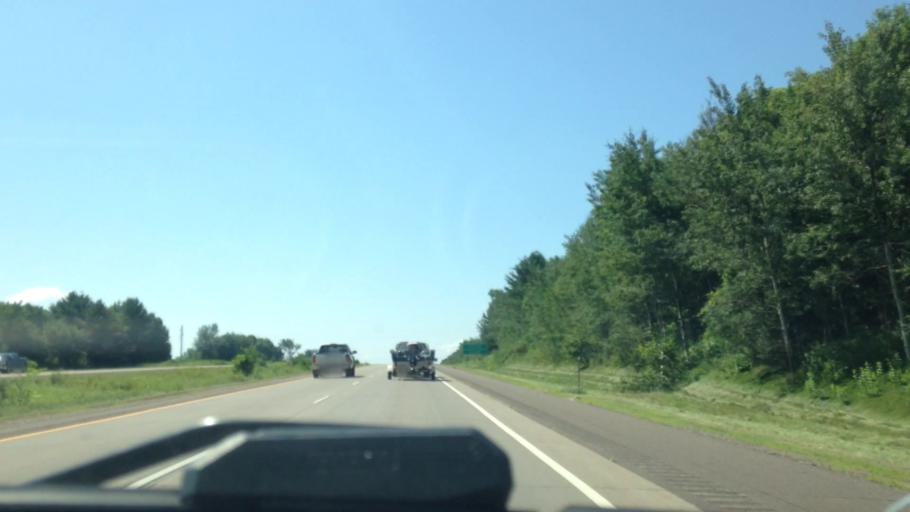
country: US
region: Wisconsin
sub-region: Barron County
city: Rice Lake
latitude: 45.4904
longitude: -91.7631
